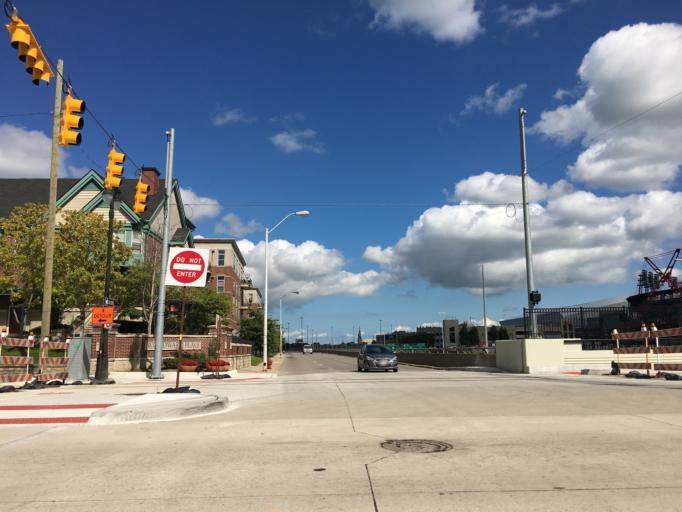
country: US
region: Michigan
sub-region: Wayne County
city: Detroit
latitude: 42.3402
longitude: -83.0531
